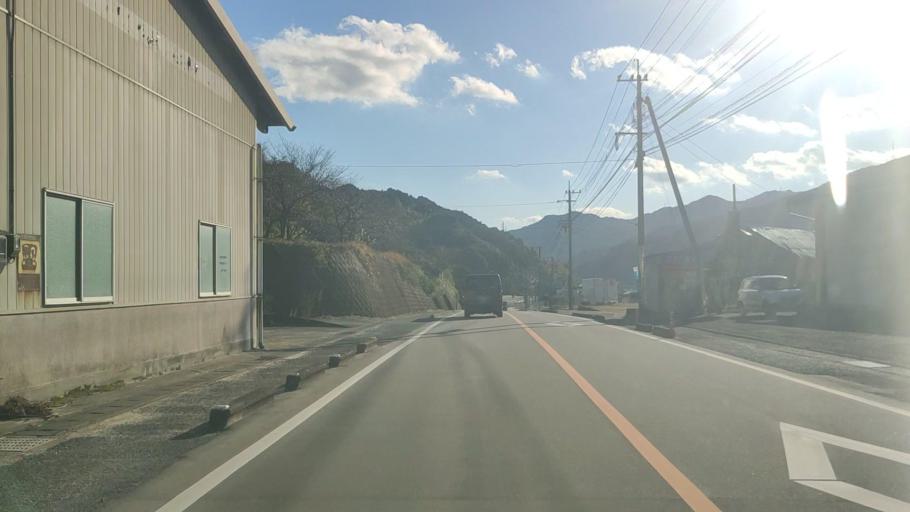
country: JP
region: Saga Prefecture
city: Saga-shi
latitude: 33.3624
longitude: 130.2541
